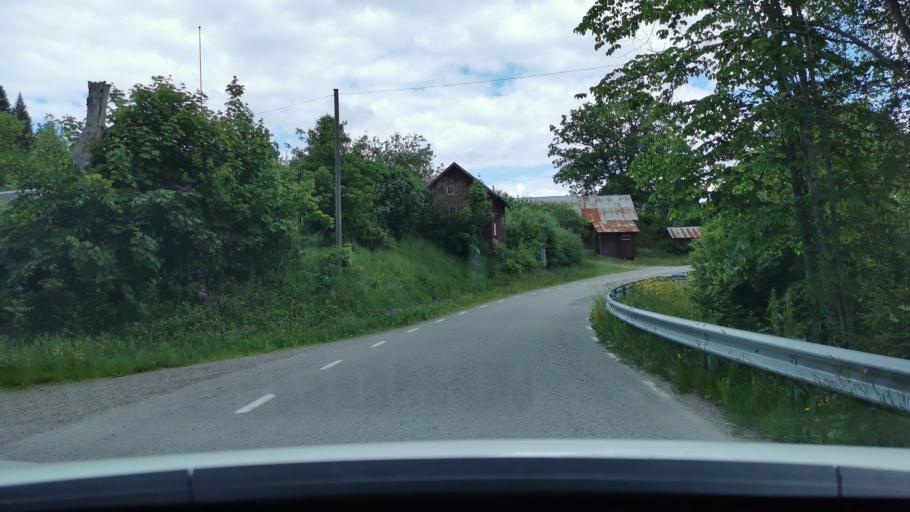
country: SE
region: Vaestra Goetaland
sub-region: Bengtsfors Kommun
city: Dals Langed
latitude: 58.8396
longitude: 12.3308
